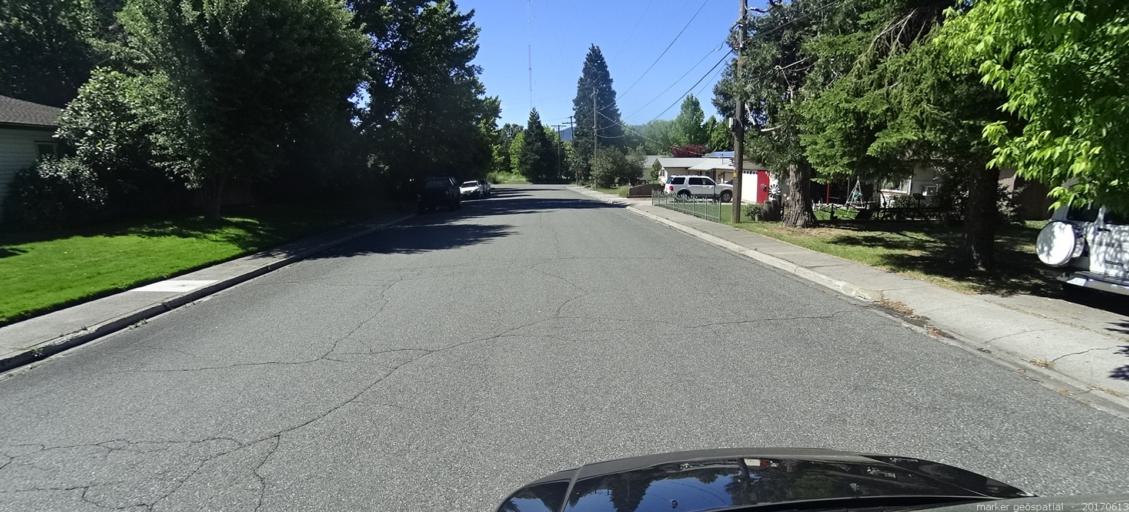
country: US
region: California
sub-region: Siskiyou County
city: Mount Shasta
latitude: 41.3207
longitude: -122.3105
